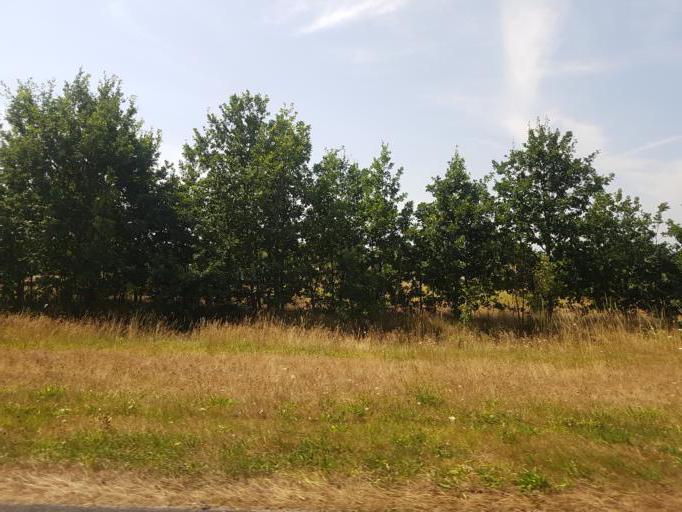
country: NL
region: Overijssel
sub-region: Gemeente Steenwijkerland
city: Steenwijk
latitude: 52.7809
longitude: 6.1211
